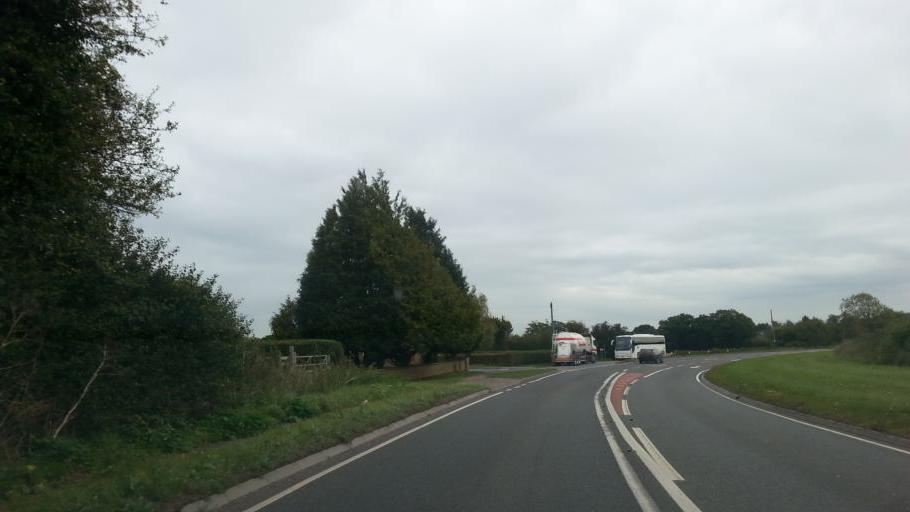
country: GB
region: England
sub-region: Gloucestershire
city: Newent
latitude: 51.8664
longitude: -2.3691
